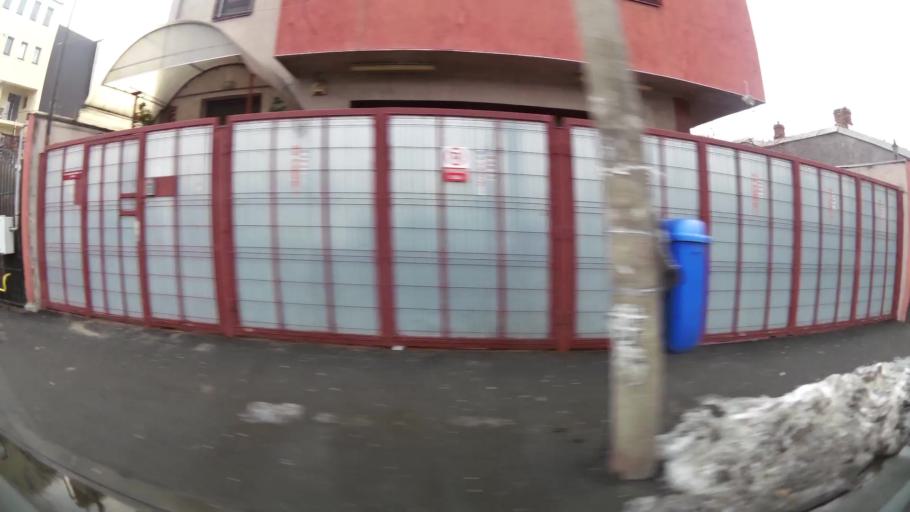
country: RO
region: Ilfov
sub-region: Comuna Fundeni-Dobroesti
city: Fundeni
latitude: 44.4753
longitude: 26.1591
